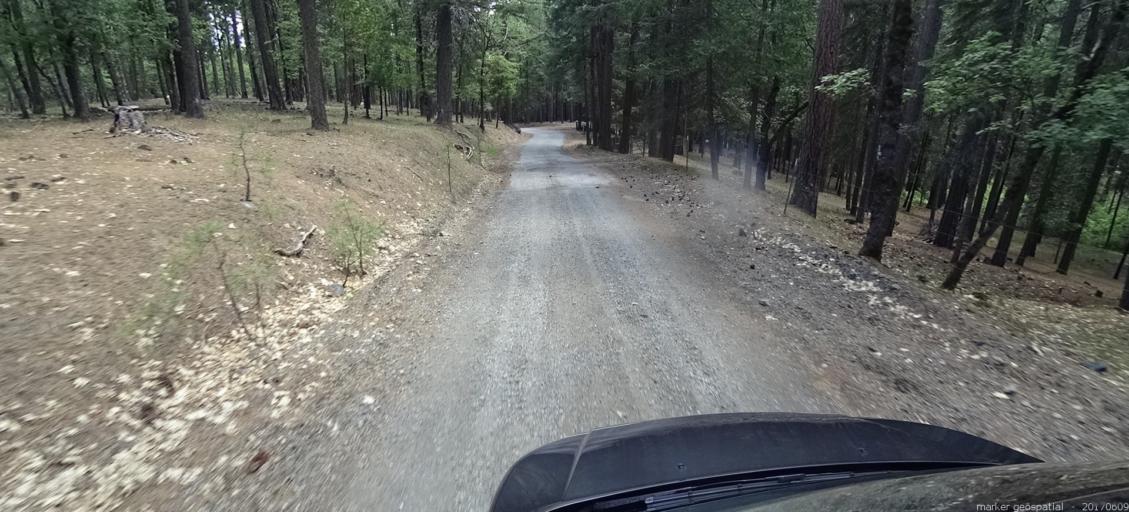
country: US
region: California
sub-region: Siskiyou County
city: Yreka
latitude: 41.3523
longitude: -122.9041
